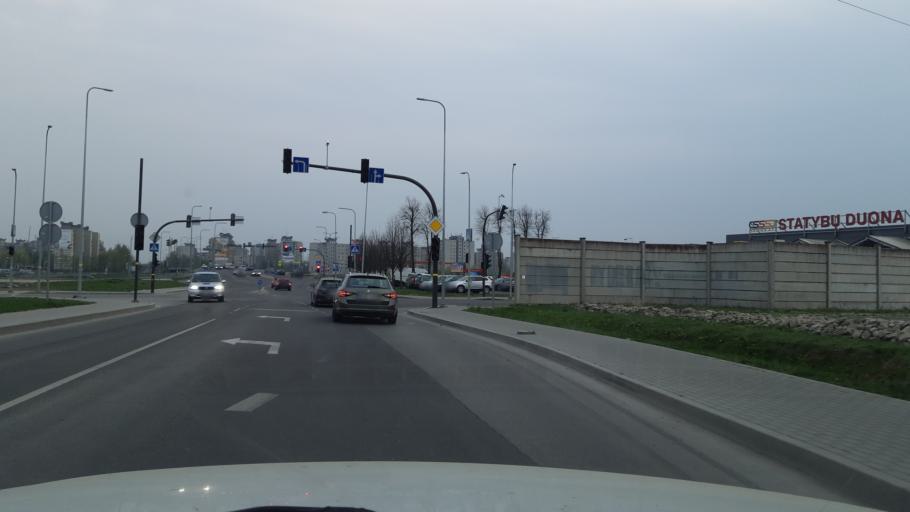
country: LT
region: Kauno apskritis
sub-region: Kaunas
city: Silainiai
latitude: 54.9399
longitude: 23.9000
